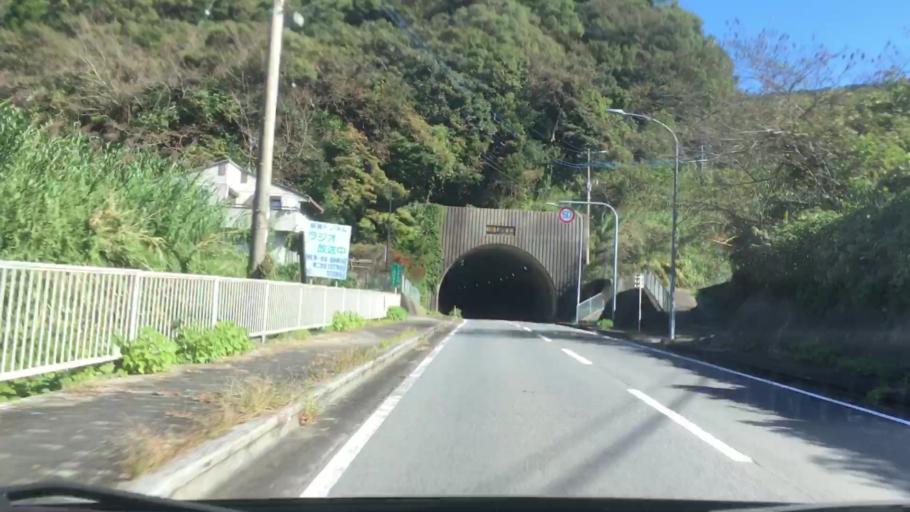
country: JP
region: Nagasaki
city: Sasebo
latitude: 32.9493
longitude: 129.6404
